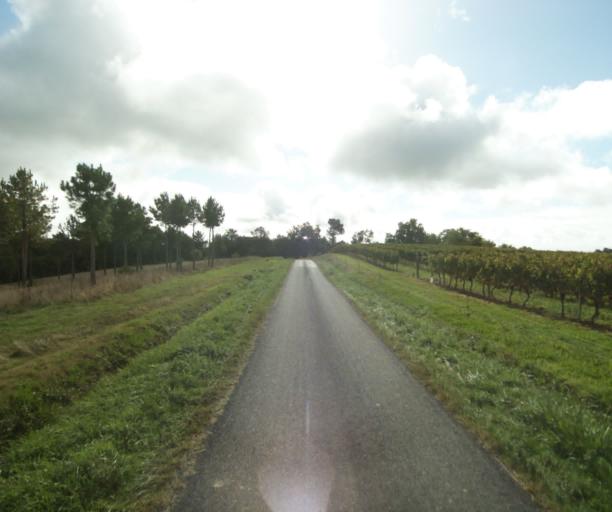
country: FR
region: Midi-Pyrenees
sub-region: Departement du Gers
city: Cazaubon
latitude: 43.8472
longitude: -0.0772
